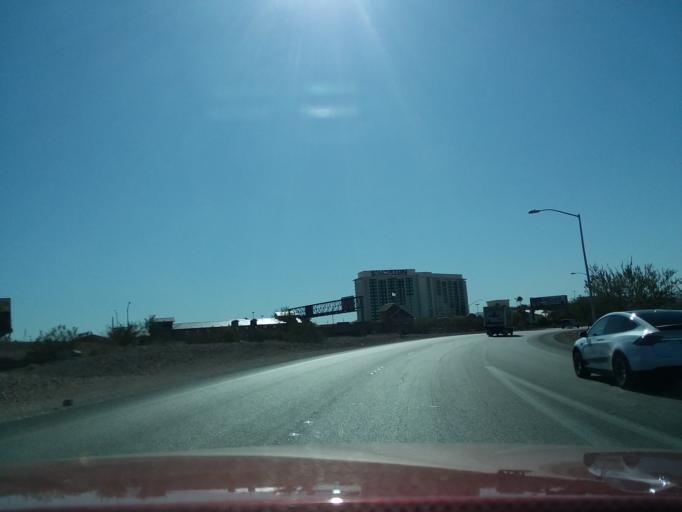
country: US
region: Nevada
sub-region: Clark County
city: Enterprise
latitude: 36.0444
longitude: -115.1822
